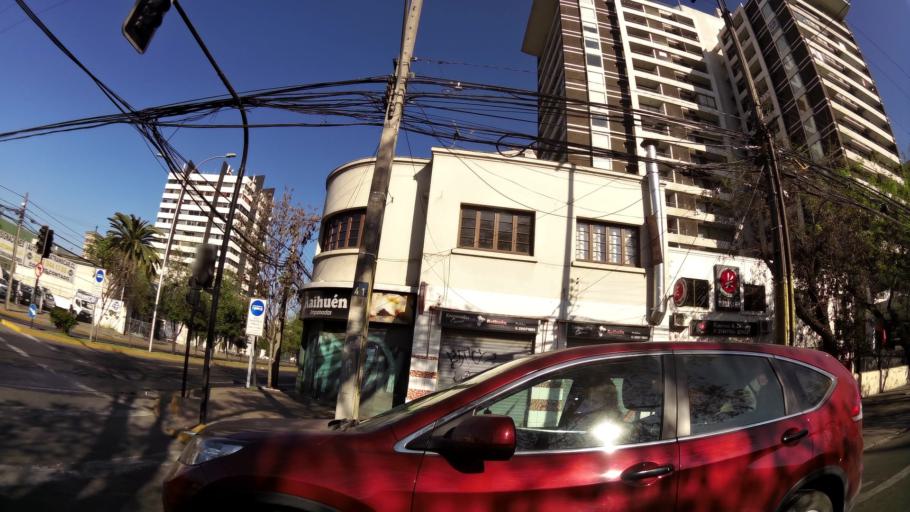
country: CL
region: Santiago Metropolitan
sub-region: Provincia de Santiago
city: Villa Presidente Frei, Nunoa, Santiago, Chile
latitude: -33.4552
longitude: -70.5920
